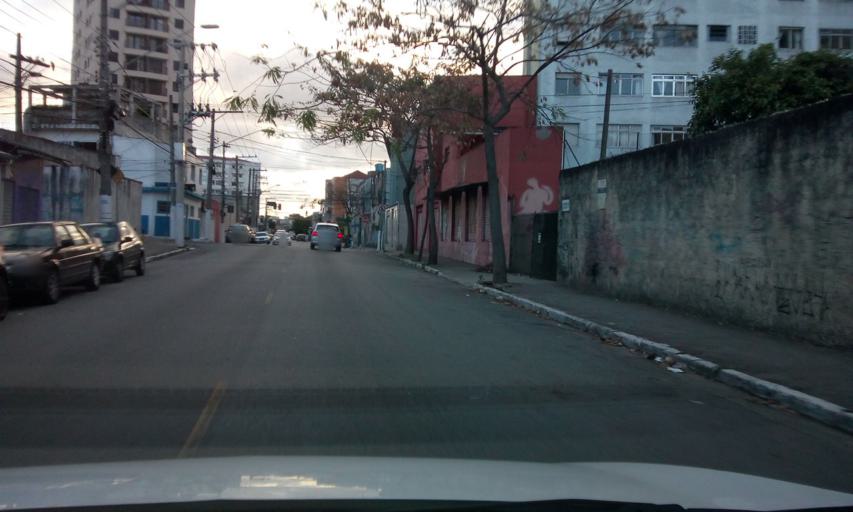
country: BR
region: Sao Paulo
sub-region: Sao Paulo
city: Sao Paulo
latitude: -23.5391
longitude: -46.5948
